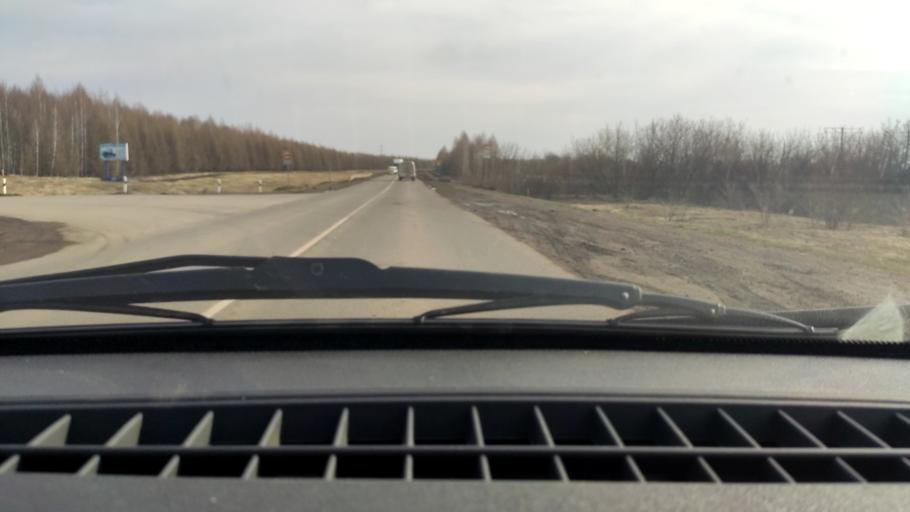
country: RU
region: Bashkortostan
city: Chishmy
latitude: 54.5750
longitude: 55.3587
